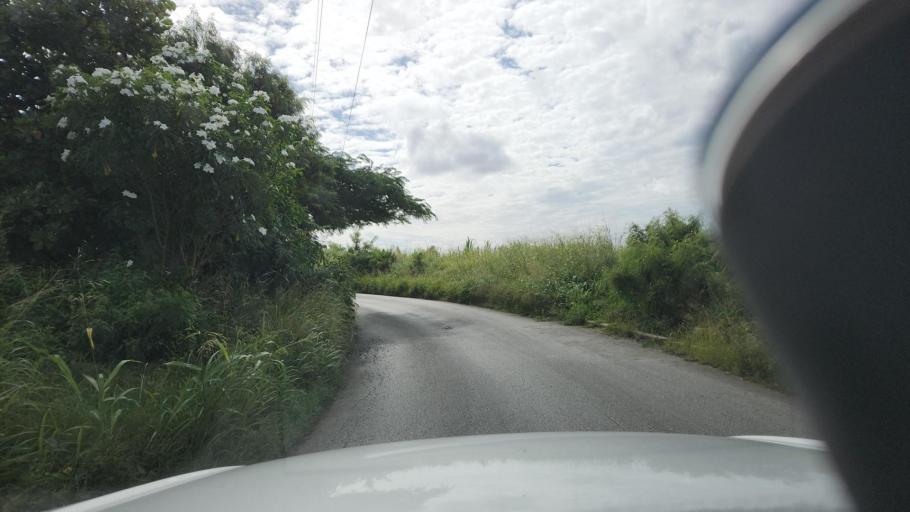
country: BB
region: Saint Lucy
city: Checker Hall
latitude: 13.2827
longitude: -59.6311
